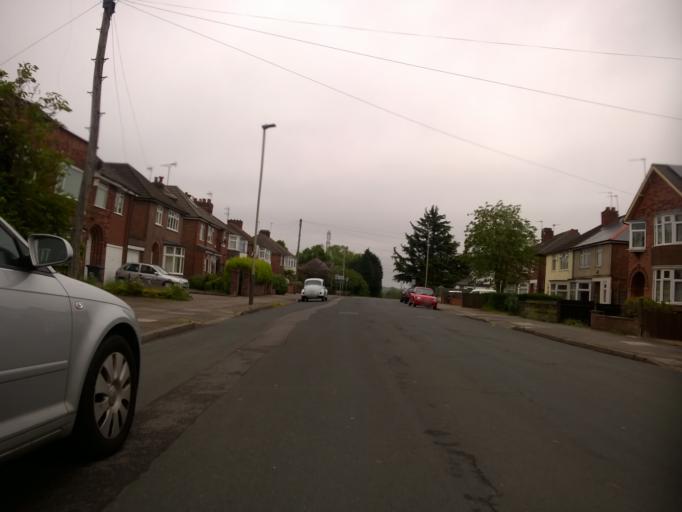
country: GB
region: England
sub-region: City of Leicester
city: Leicester
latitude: 52.6177
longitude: -1.1547
